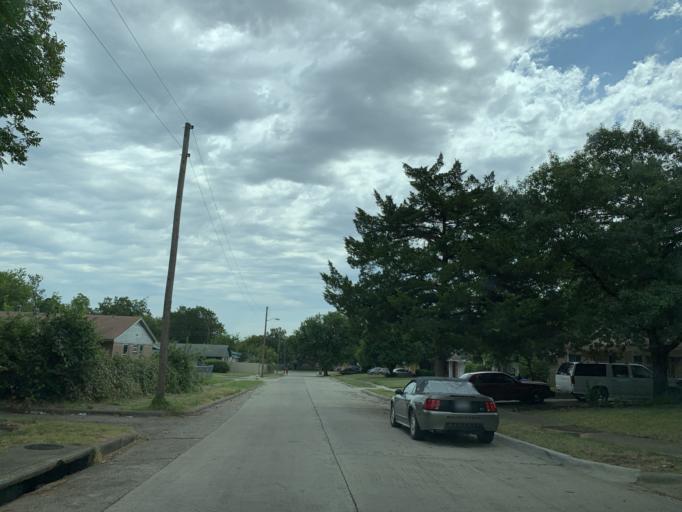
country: US
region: Texas
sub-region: Dallas County
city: DeSoto
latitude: 32.6628
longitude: -96.8285
